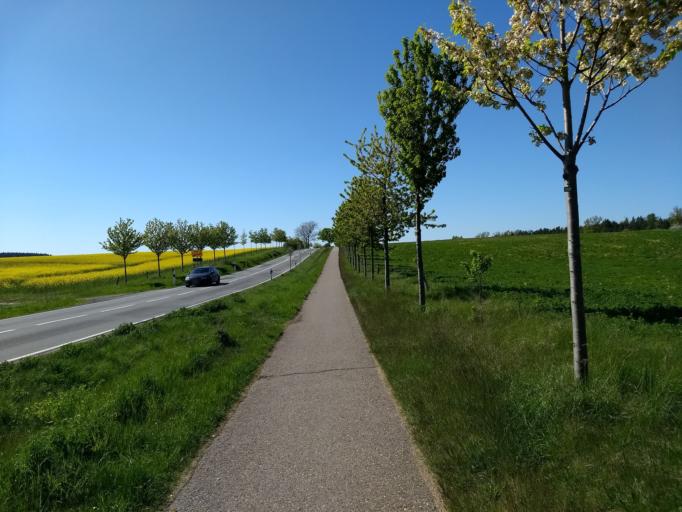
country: DE
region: Mecklenburg-Vorpommern
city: Waren
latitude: 53.5292
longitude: 12.6380
